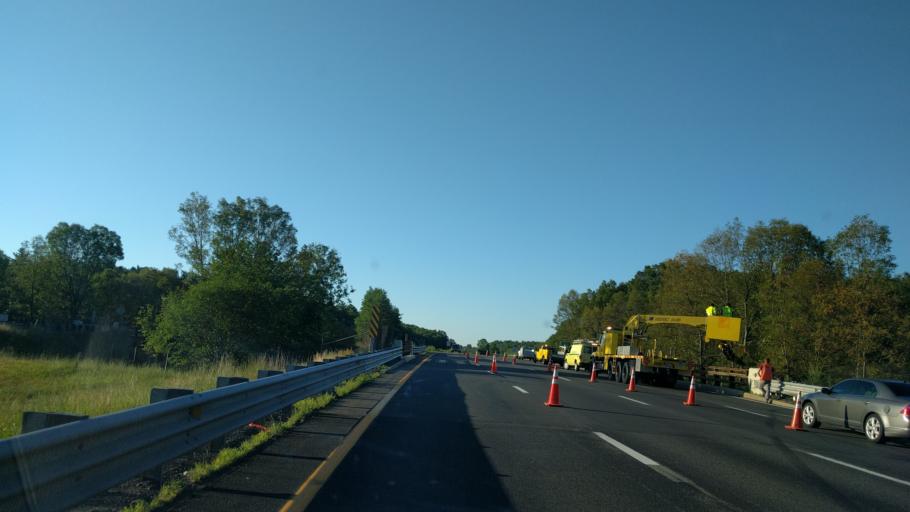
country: US
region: Massachusetts
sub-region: Norfolk County
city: Franklin
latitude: 42.0880
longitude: -71.4256
